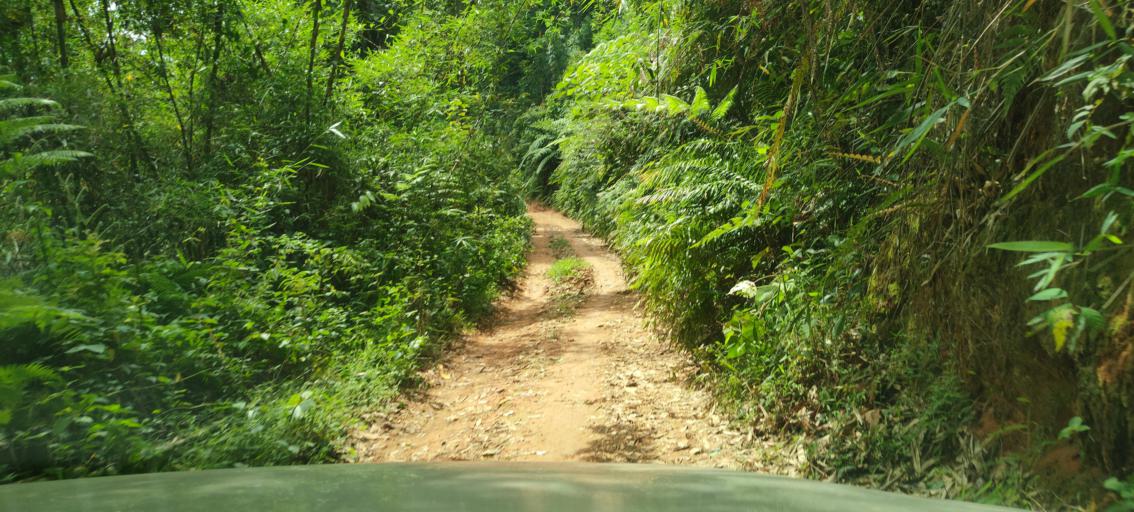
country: LA
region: Loungnamtha
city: Muang Nale
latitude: 20.4187
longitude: 101.4647
